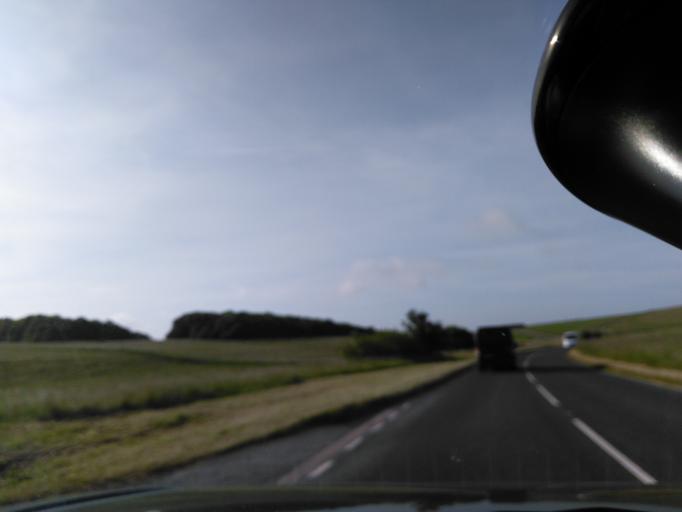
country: GB
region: England
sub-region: Wiltshire
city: Shrewton
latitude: 51.2165
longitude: -1.9411
